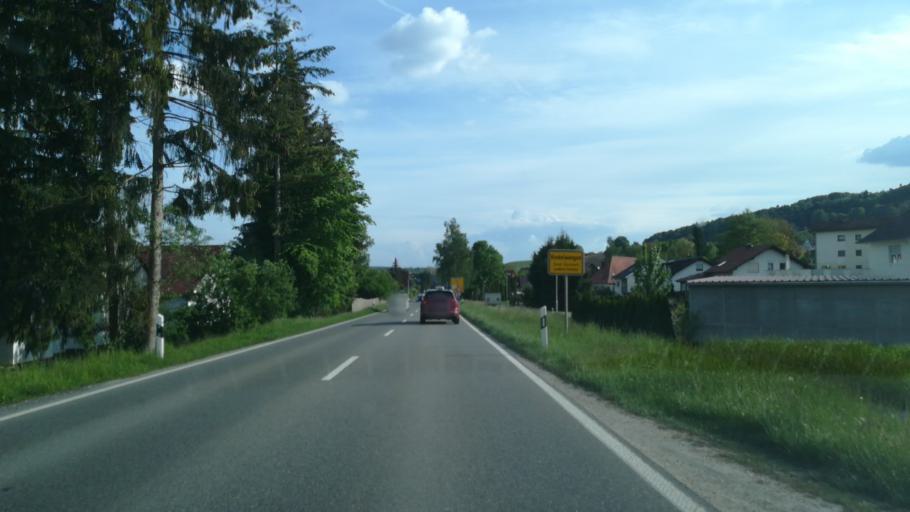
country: DE
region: Baden-Wuerttemberg
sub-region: Freiburg Region
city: Stockach
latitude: 47.8637
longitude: 9.0050
